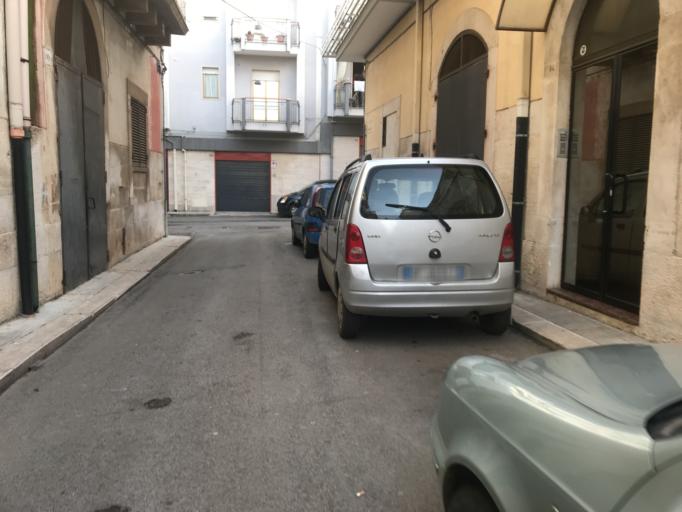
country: IT
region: Apulia
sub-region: Provincia di Bari
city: Corato
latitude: 41.1504
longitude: 16.4168
